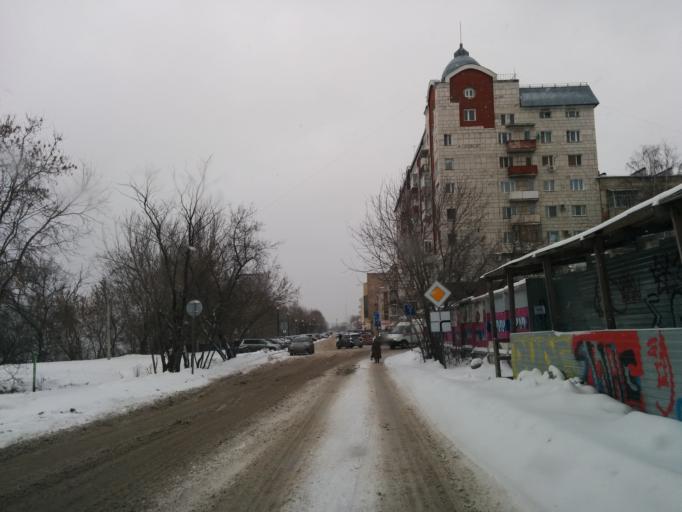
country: RU
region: Perm
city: Perm
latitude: 58.0154
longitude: 56.2260
